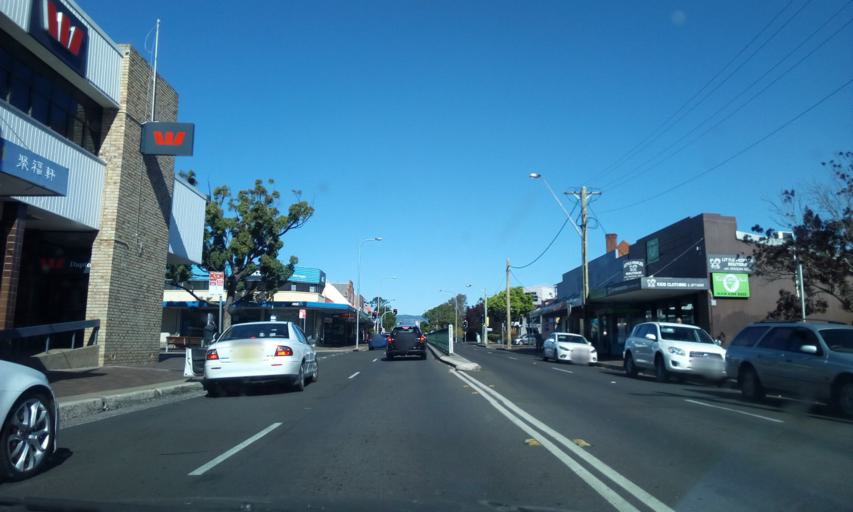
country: AU
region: New South Wales
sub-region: Wollongong
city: Dapto
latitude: -34.4935
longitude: 150.7947
